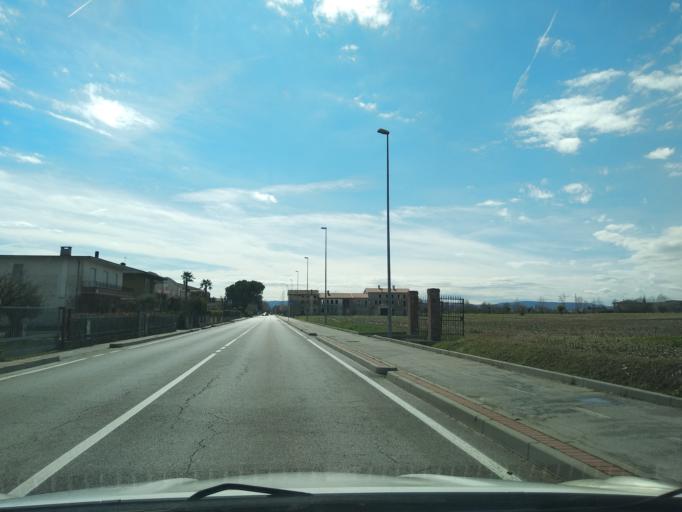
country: IT
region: Veneto
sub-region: Provincia di Vicenza
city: Monticello Conte Otto
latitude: 45.5930
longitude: 11.5800
